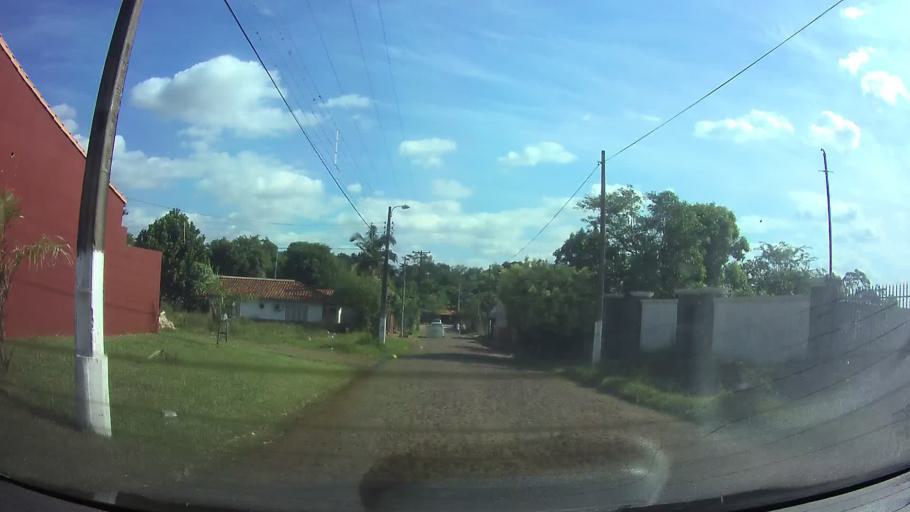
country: PY
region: Central
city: Limpio
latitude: -25.2530
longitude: -57.4710
